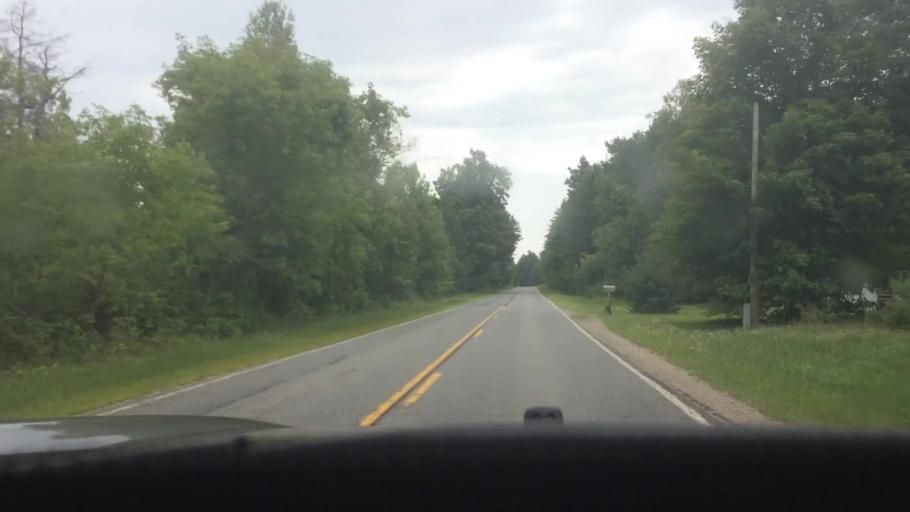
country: US
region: New York
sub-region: St. Lawrence County
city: Hannawa Falls
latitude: 44.5985
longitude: -74.8868
